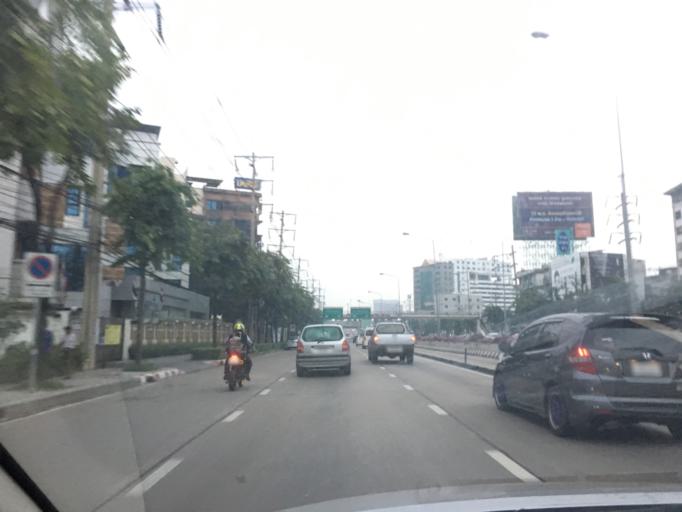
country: TH
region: Bangkok
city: Bang Kho Laem
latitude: 13.6918
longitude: 100.5019
